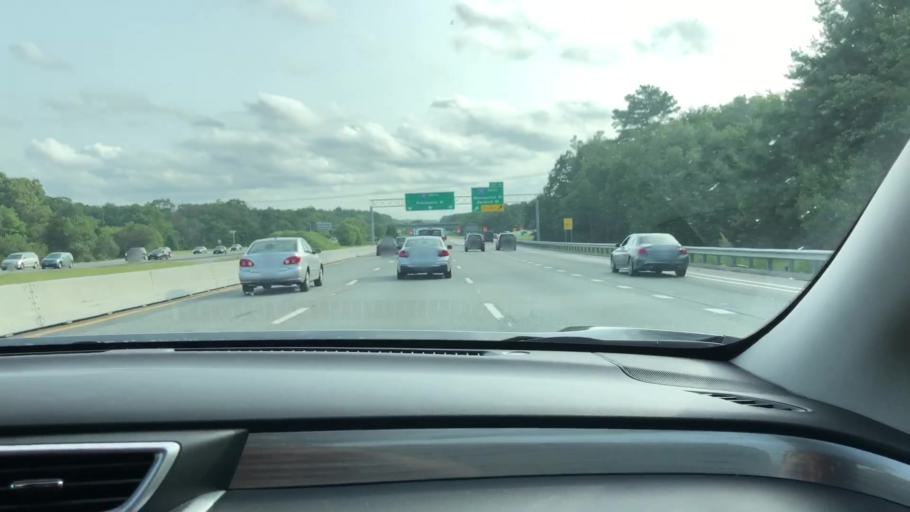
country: US
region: Massachusetts
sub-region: Bristol County
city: Attleboro
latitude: 41.9597
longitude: -71.3016
